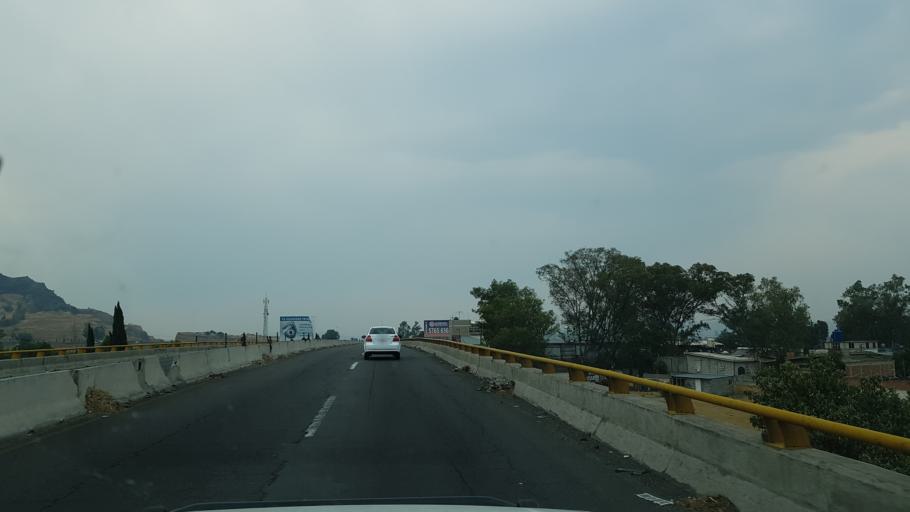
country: MX
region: Mexico
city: Cocotitlan
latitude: 19.2357
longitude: -98.8497
